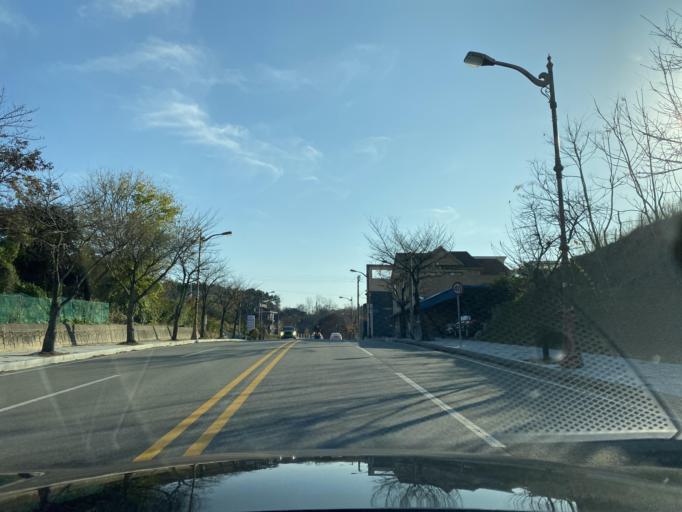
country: KR
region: Chungcheongnam-do
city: Yesan
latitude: 36.6849
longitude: 126.8360
